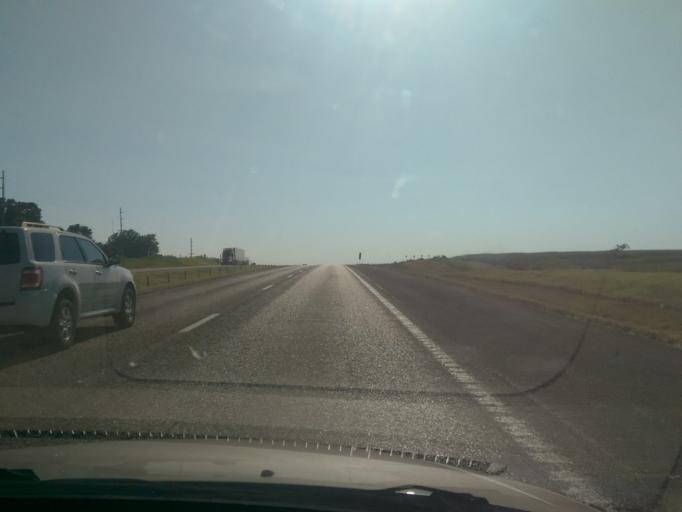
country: US
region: Missouri
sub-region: Lafayette County
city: Concordia
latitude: 38.9936
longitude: -93.5996
